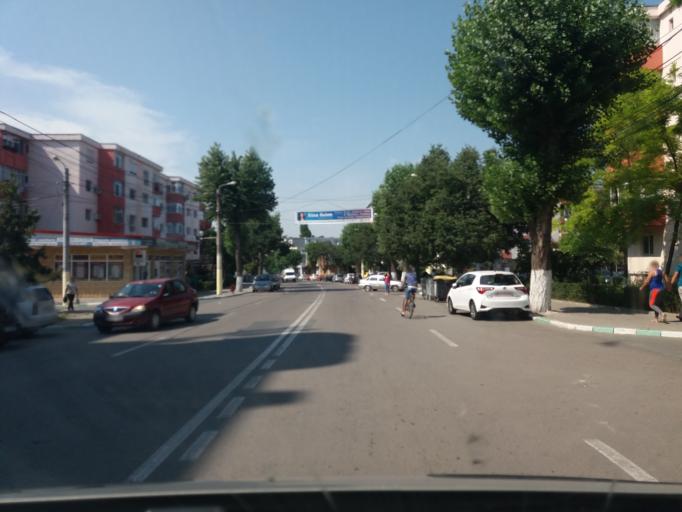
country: RO
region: Constanta
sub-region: Comuna Navodari
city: Navodari
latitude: 44.3179
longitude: 28.6093
